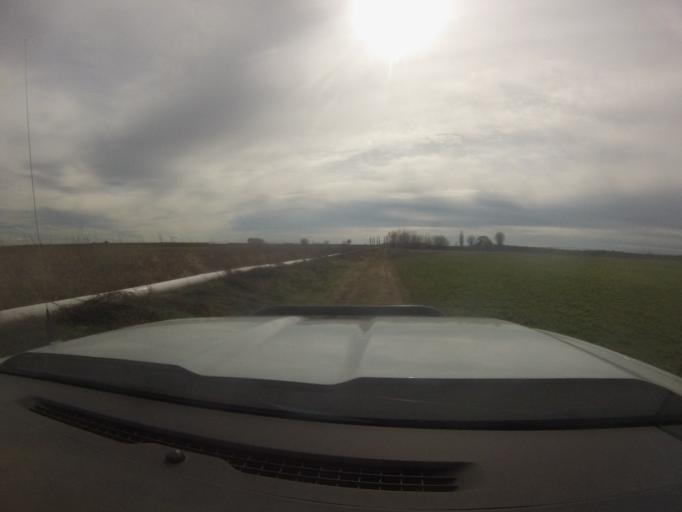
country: US
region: Washington
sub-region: Franklin County
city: Basin City
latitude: 46.6038
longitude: -119.0475
